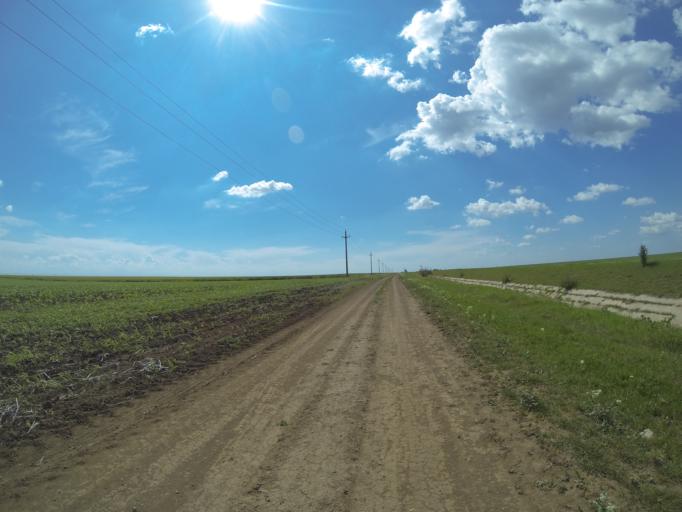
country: RO
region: Dolj
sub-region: Comuna Segarcea
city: Segarcea
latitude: 44.0195
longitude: 23.7578
